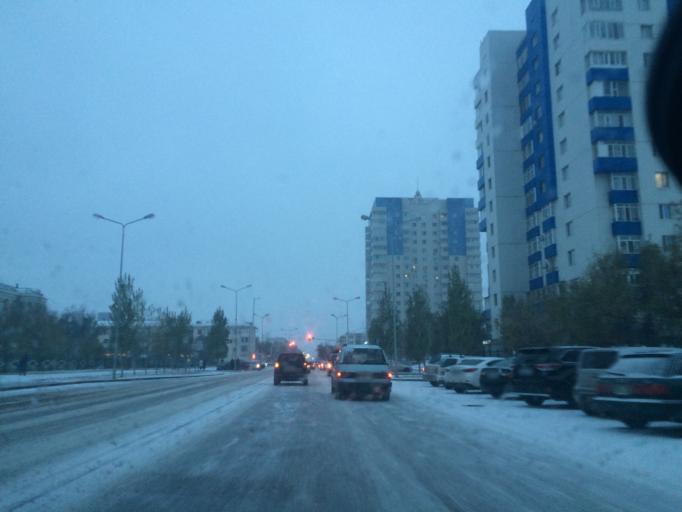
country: KZ
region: Astana Qalasy
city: Astana
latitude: 51.1856
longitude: 71.4107
